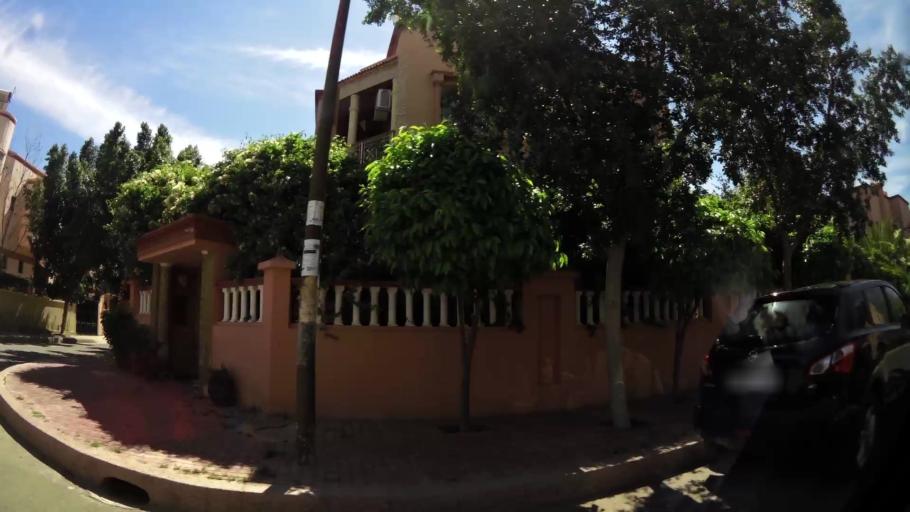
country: MA
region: Marrakech-Tensift-Al Haouz
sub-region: Marrakech
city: Marrakesh
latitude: 31.6758
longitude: -8.0014
